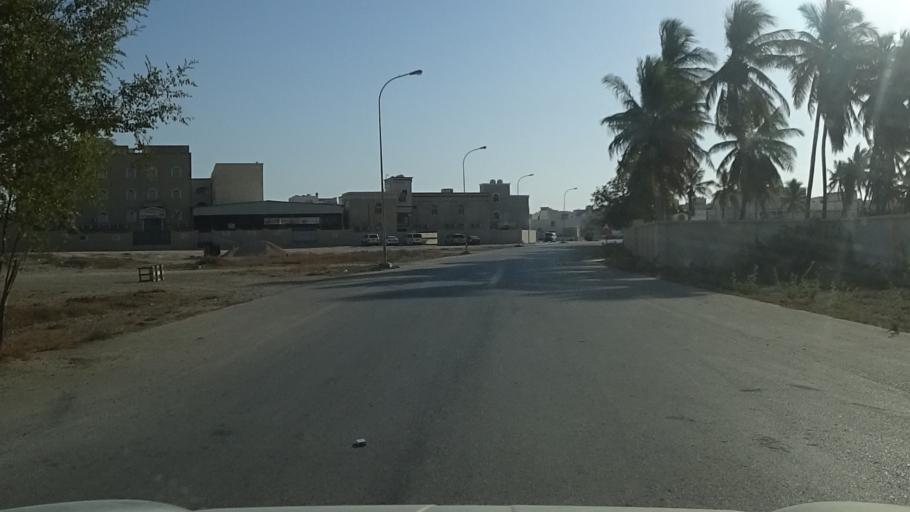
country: OM
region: Zufar
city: Salalah
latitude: 17.0206
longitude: 54.1541
